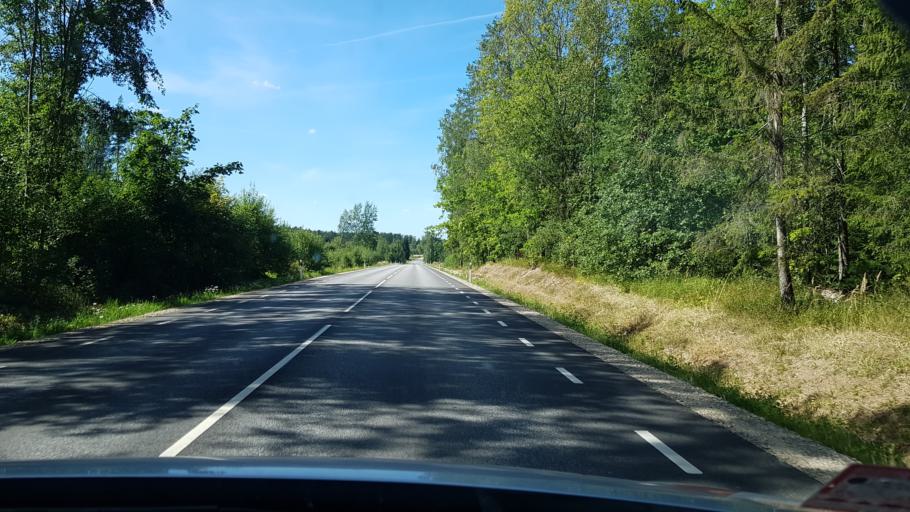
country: EE
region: Polvamaa
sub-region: Polva linn
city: Polva
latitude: 58.0092
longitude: 27.1916
